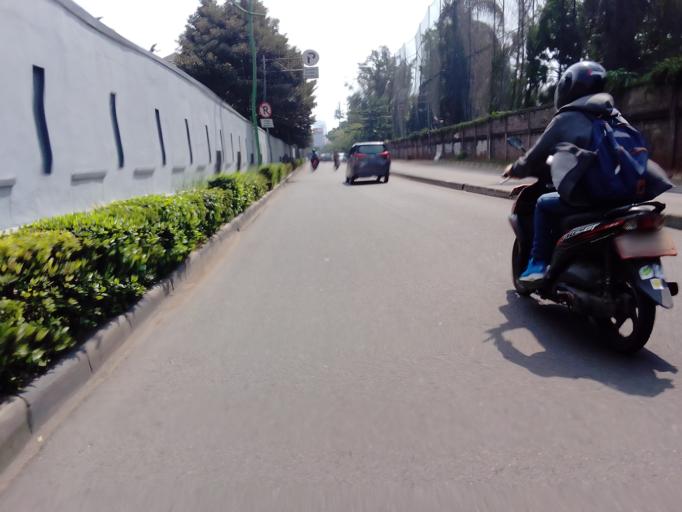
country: ID
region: Jakarta Raya
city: Jakarta
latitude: -6.2207
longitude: 106.7951
